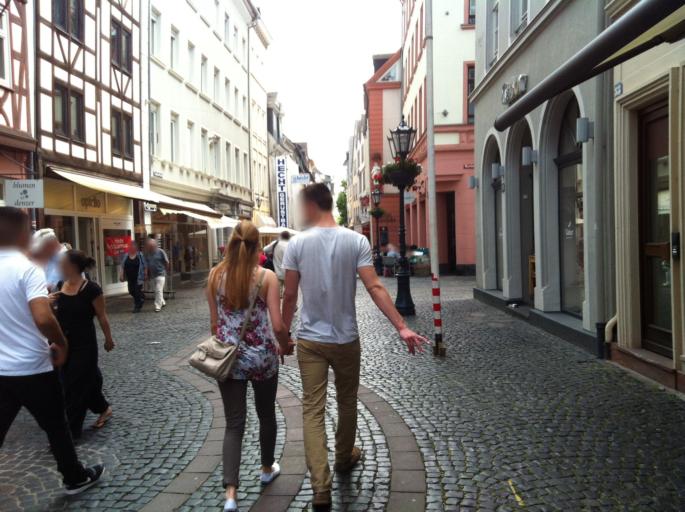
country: DE
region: Rheinland-Pfalz
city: Mainz
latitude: 49.9969
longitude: 8.2748
